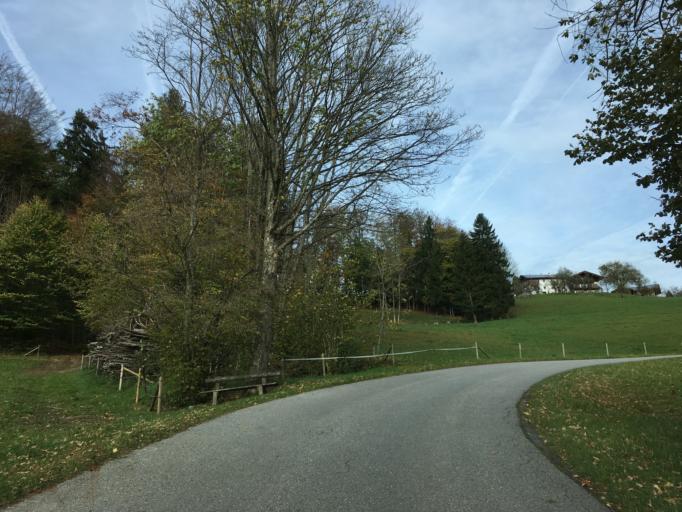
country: DE
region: Bavaria
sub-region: Upper Bavaria
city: Samerberg
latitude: 47.7670
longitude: 12.1881
